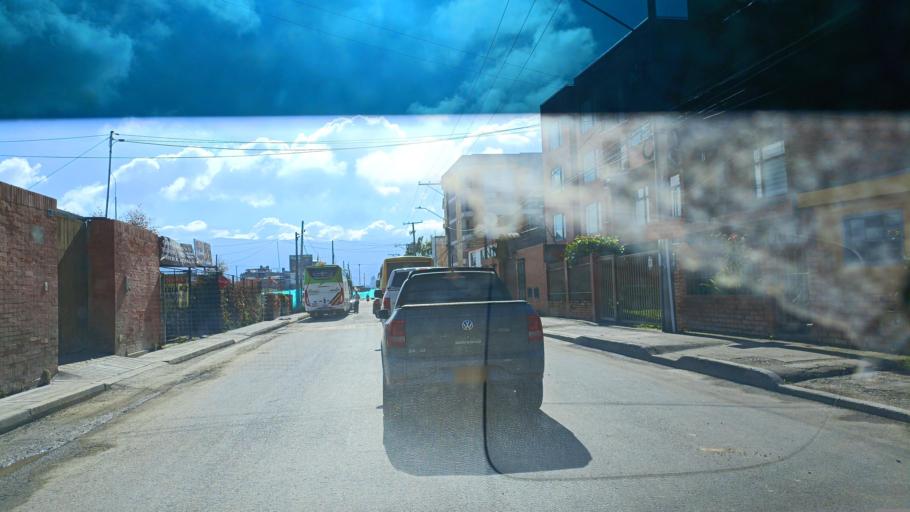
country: CO
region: Cundinamarca
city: Cajica
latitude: 4.9118
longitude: -74.0268
